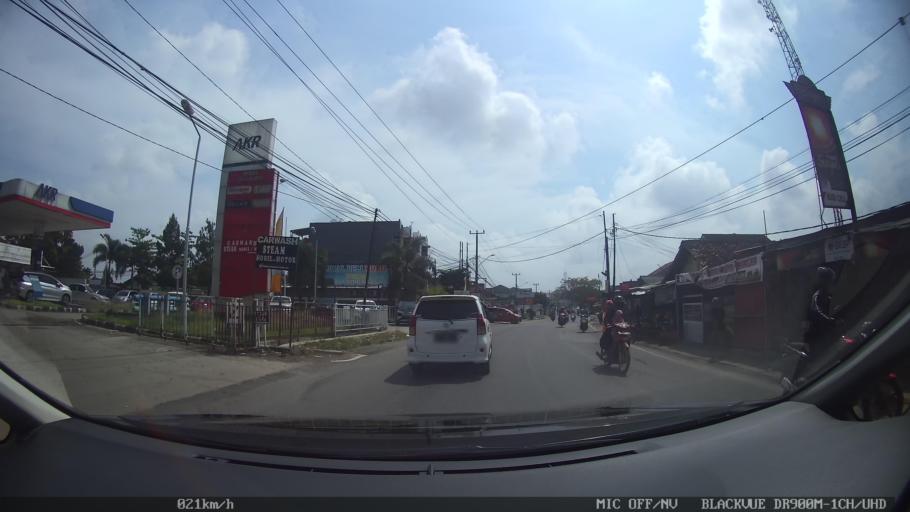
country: ID
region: Lampung
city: Kedaton
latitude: -5.3644
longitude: 105.2759
